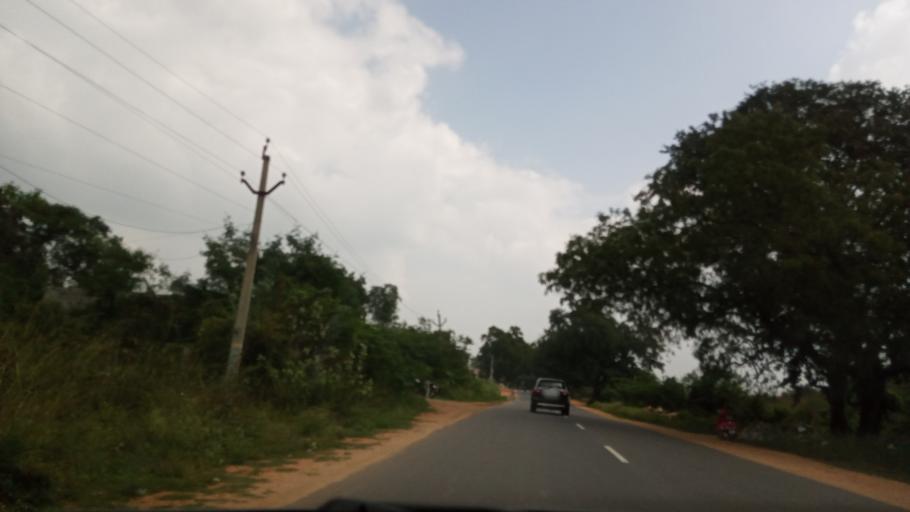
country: IN
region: Andhra Pradesh
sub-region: Chittoor
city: Madanapalle
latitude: 13.6365
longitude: 78.6392
